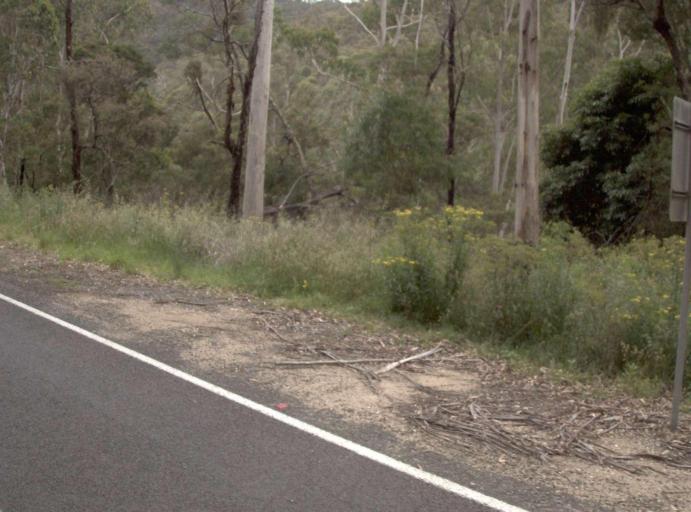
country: AU
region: New South Wales
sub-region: Bombala
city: Bombala
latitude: -37.4165
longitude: 149.1986
